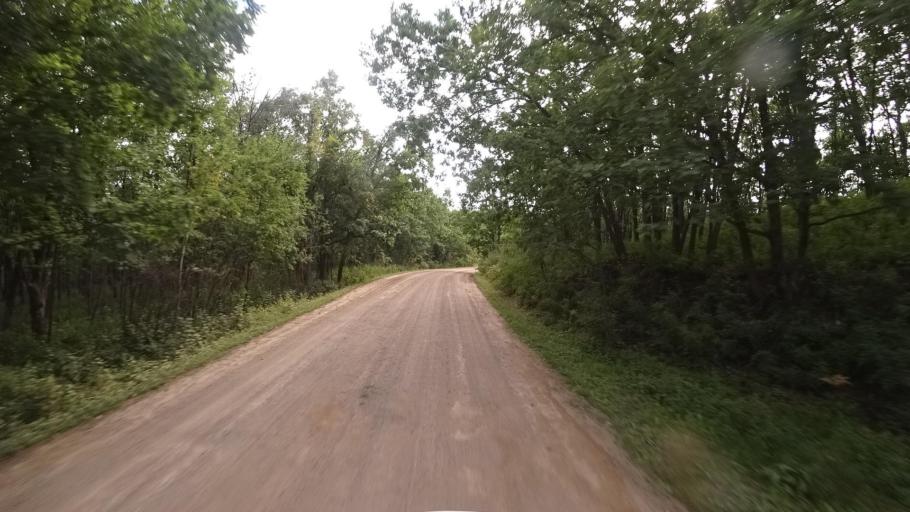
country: RU
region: Primorskiy
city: Dostoyevka
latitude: 44.3489
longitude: 133.5193
